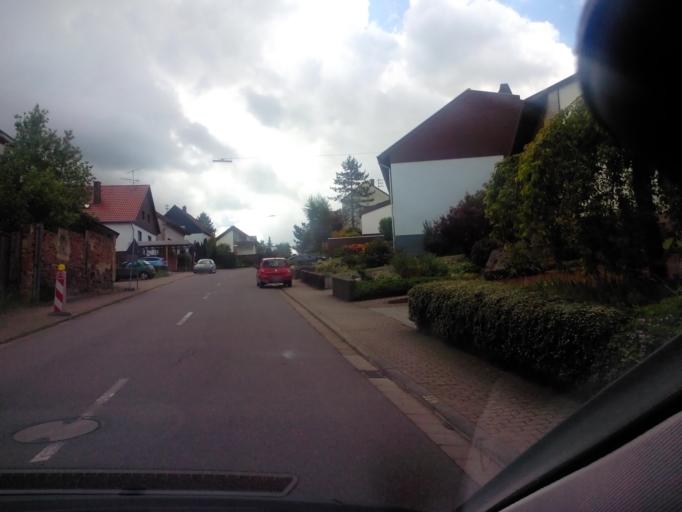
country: DE
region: Saarland
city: Heusweiler
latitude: 49.3592
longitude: 6.8747
